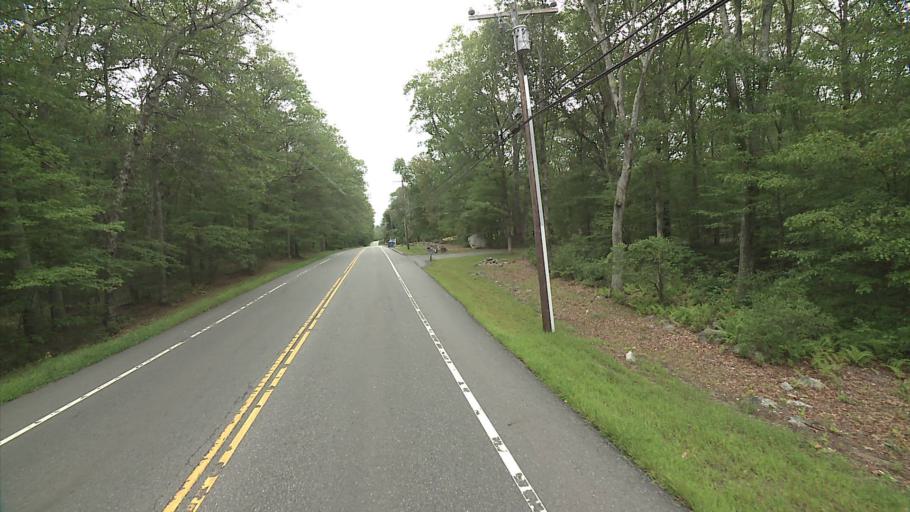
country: US
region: Connecticut
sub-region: New London County
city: Colchester
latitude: 41.6051
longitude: -72.3438
